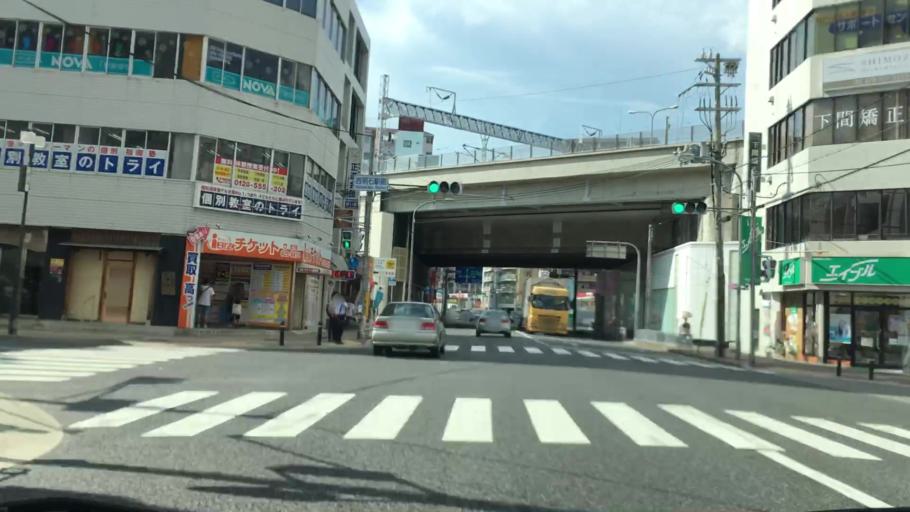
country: JP
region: Hyogo
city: Akashi
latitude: 34.6662
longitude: 134.9628
